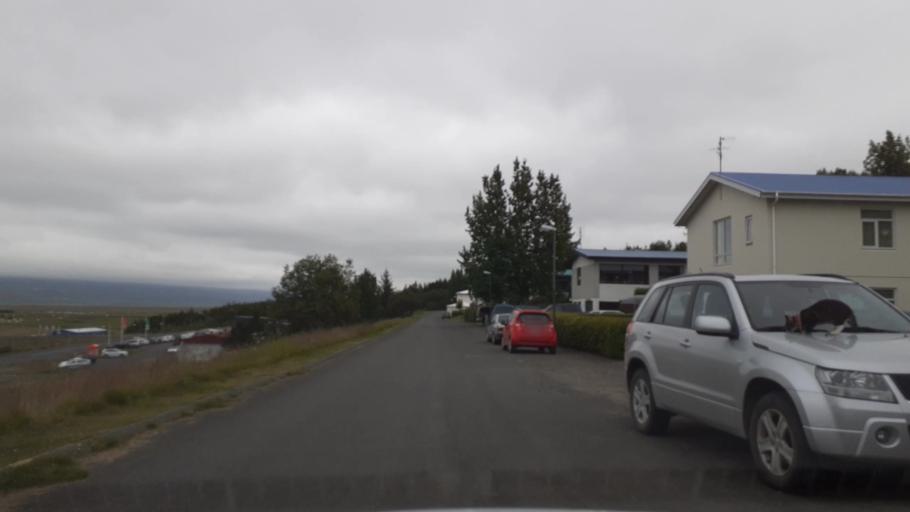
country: IS
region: Northwest
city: Saudarkrokur
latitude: 65.5548
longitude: -19.4501
